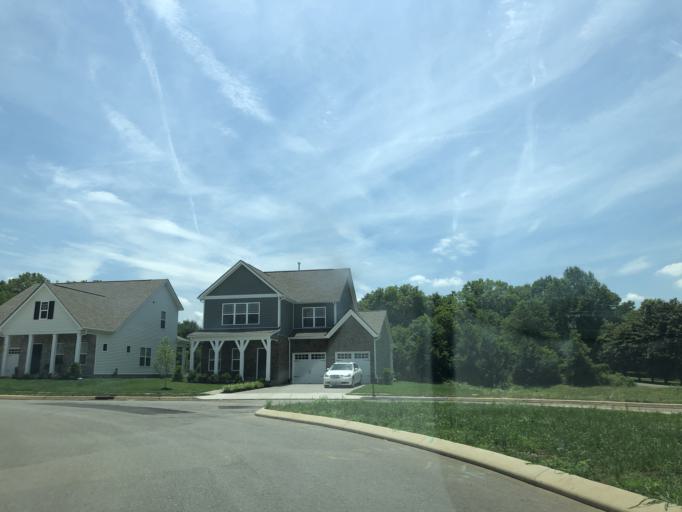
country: US
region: Tennessee
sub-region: Williamson County
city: Nolensville
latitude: 36.0270
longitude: -86.6649
